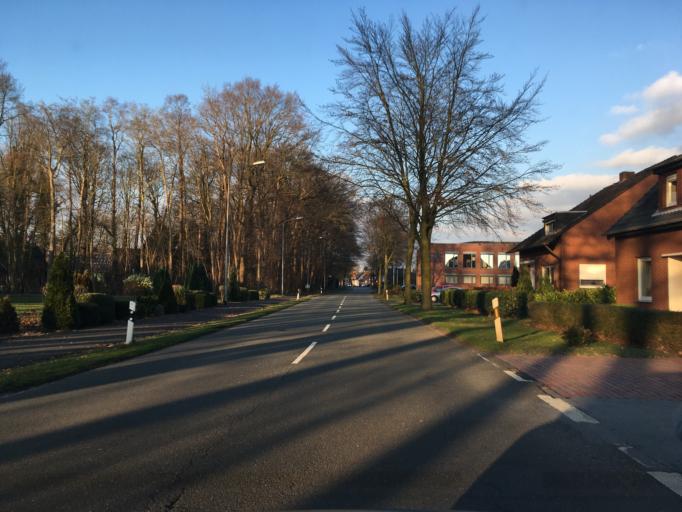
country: DE
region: North Rhine-Westphalia
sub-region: Regierungsbezirk Munster
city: Gronau
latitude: 52.1699
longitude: 7.0342
